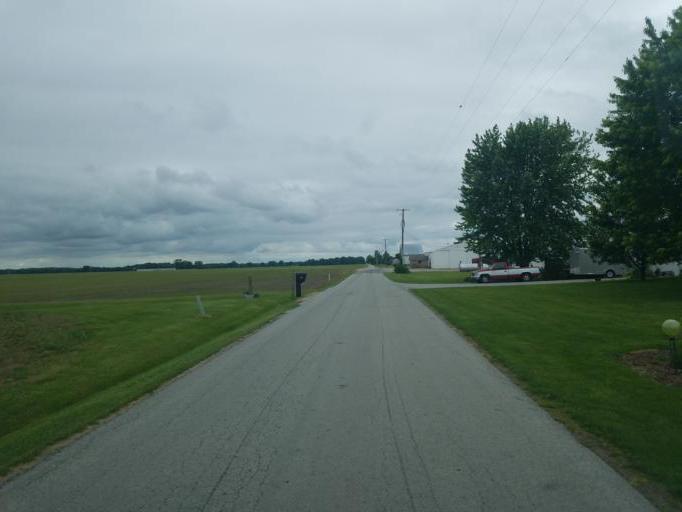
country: US
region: Ohio
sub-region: Morrow County
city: Cardington
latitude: 40.5425
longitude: -82.8835
